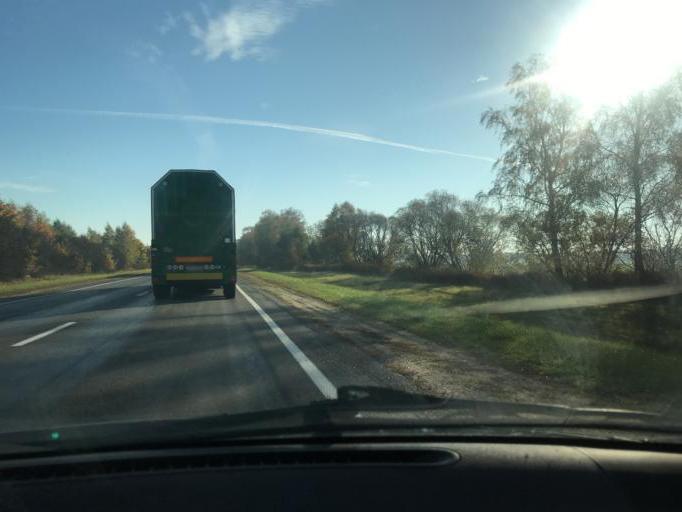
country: BY
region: Brest
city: Ivanava
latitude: 52.1485
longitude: 25.4156
